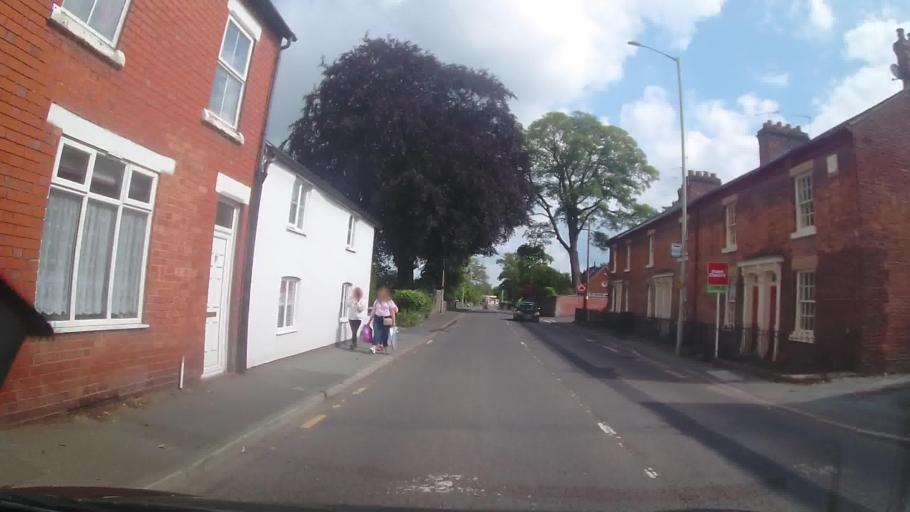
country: GB
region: England
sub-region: Shropshire
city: Oswestry
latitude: 52.8570
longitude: -3.0508
